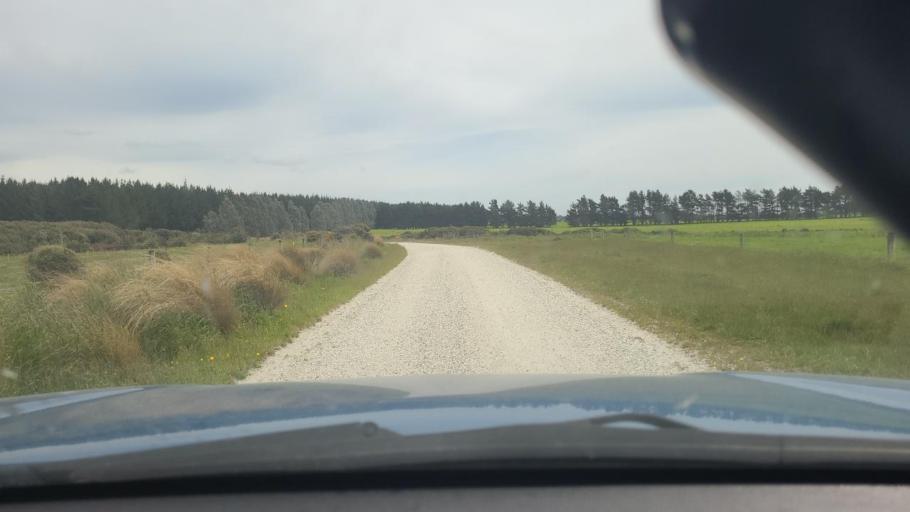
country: NZ
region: Southland
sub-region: Invercargill City
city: Bluff
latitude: -46.5436
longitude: 168.6225
